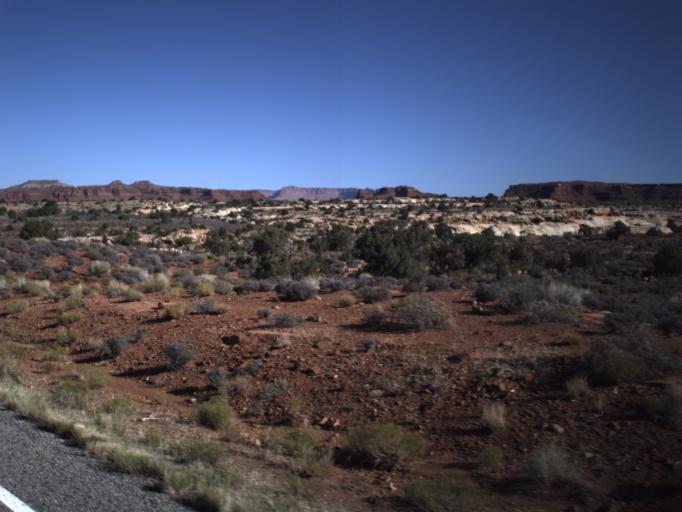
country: US
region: Utah
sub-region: San Juan County
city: Blanding
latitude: 37.7956
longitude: -110.3029
